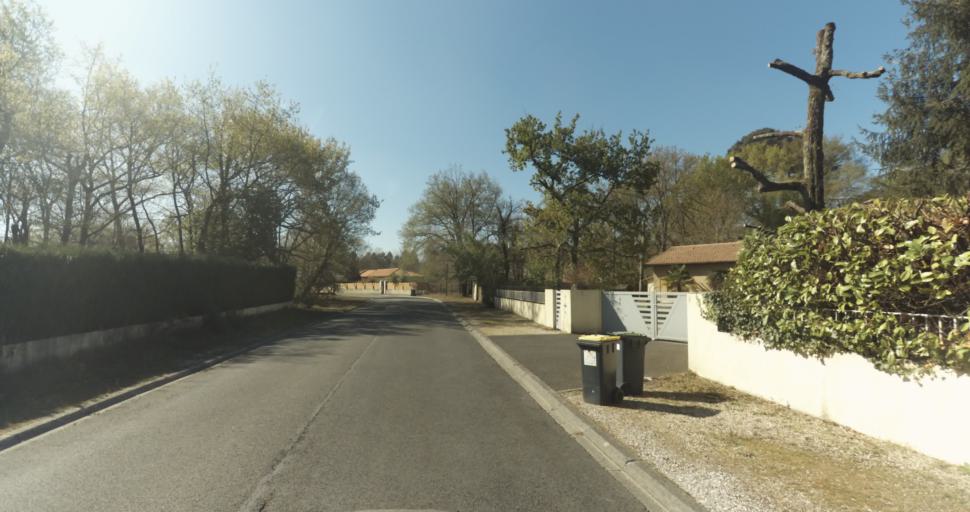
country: FR
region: Aquitaine
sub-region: Departement de la Gironde
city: Martignas-sur-Jalle
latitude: 44.7955
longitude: -0.8408
